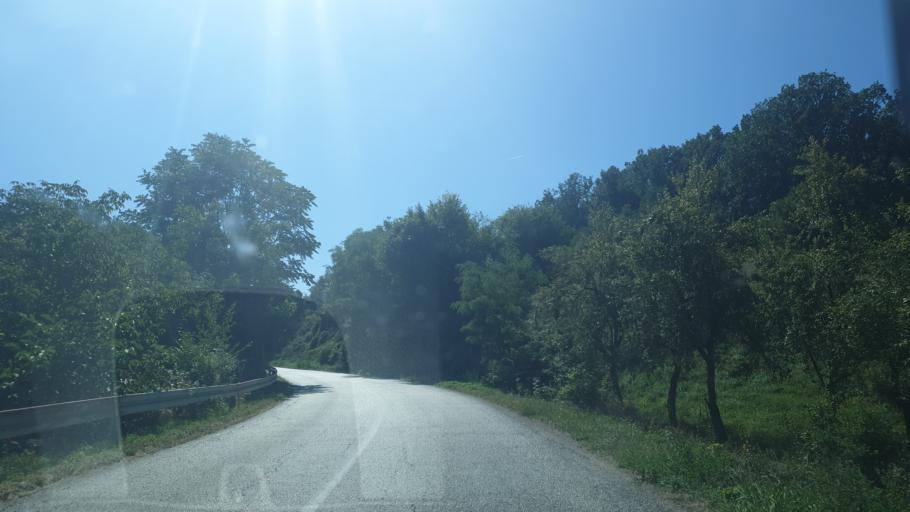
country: RS
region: Central Serbia
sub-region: Kolubarski Okrug
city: Mionica
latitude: 44.2219
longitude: 20.0866
